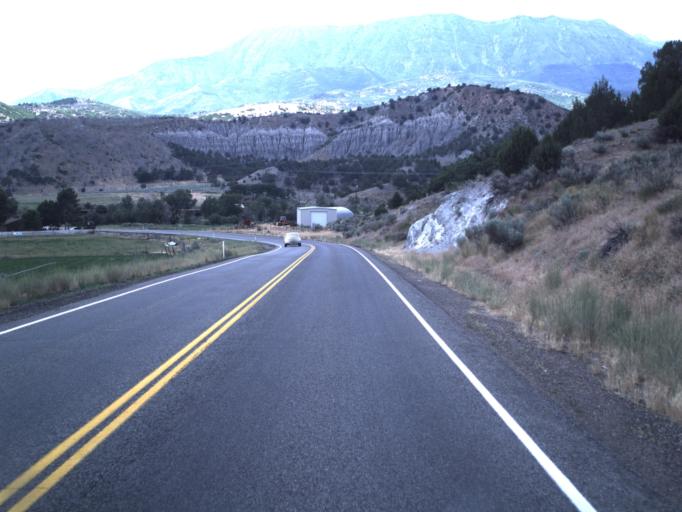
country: US
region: Utah
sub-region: Juab County
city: Nephi
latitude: 39.7160
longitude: -111.7254
